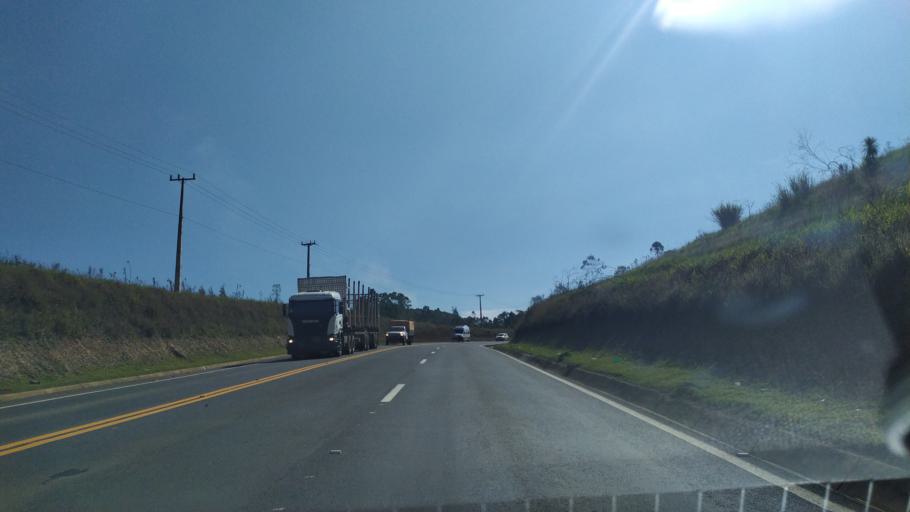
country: BR
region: Parana
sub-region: Telemaco Borba
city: Telemaco Borba
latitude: -24.2592
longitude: -50.7266
